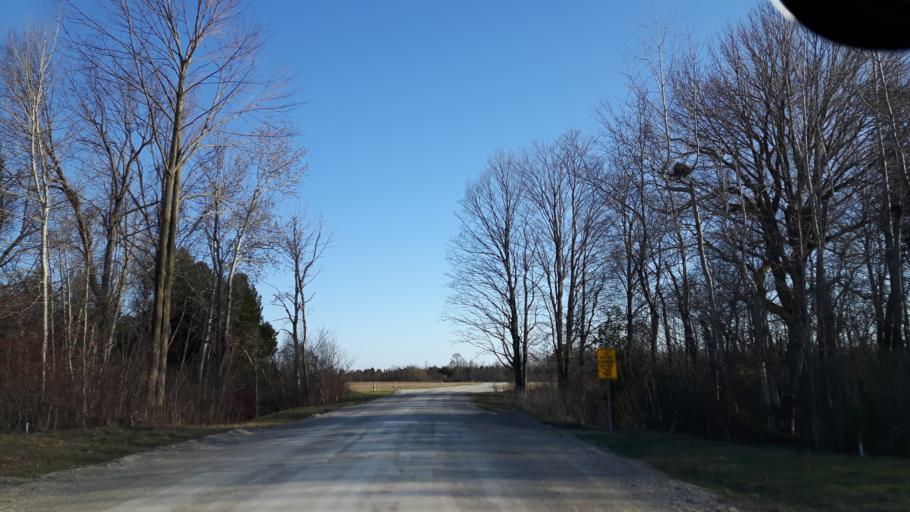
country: CA
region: Ontario
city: Goderich
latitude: 43.7256
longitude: -81.6936
